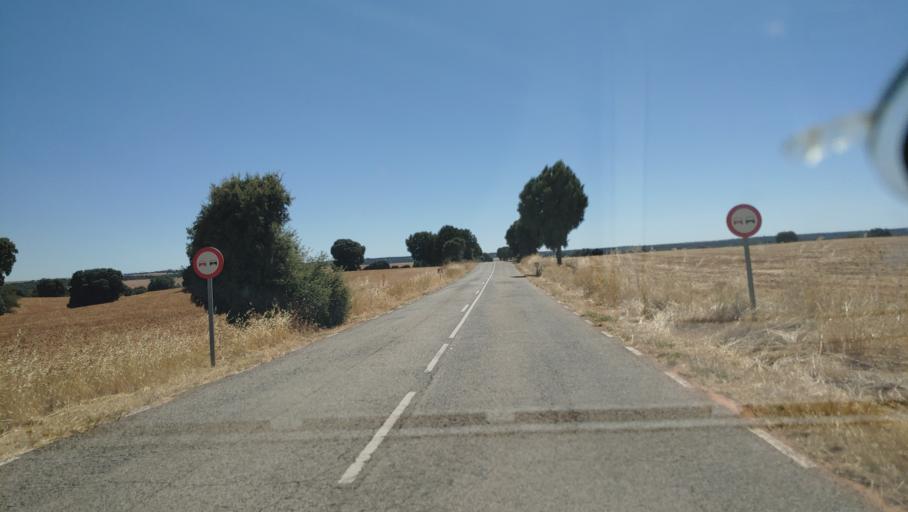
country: ES
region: Castille-La Mancha
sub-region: Provincia de Albacete
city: Ossa de Montiel
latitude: 38.9088
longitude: -2.7598
